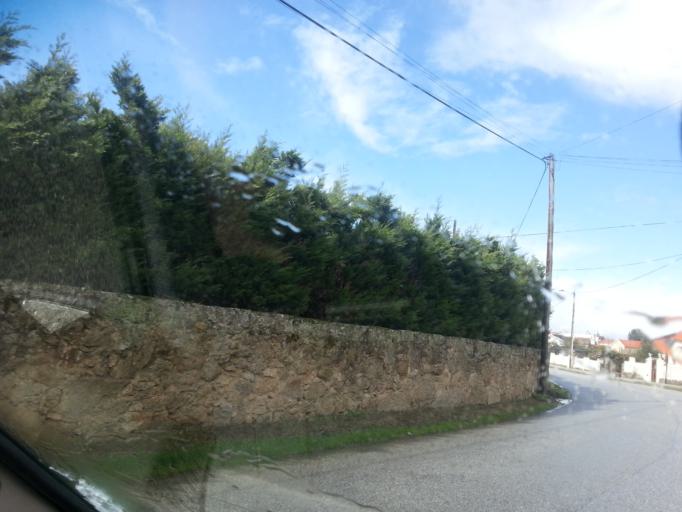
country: PT
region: Guarda
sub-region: Fornos de Algodres
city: Fornos de Algodres
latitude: 40.5575
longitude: -7.4819
